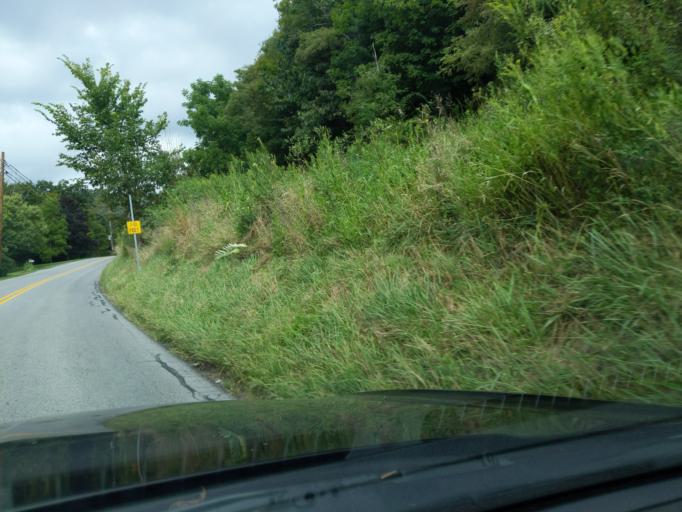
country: US
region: Pennsylvania
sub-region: Blair County
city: Claysburg
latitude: 40.3539
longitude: -78.4610
